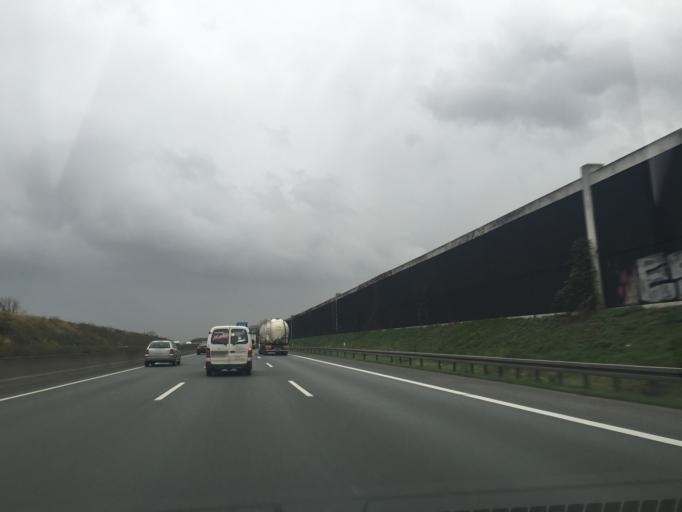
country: DE
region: North Rhine-Westphalia
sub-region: Regierungsbezirk Munster
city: Muenster
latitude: 51.9597
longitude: 7.5460
